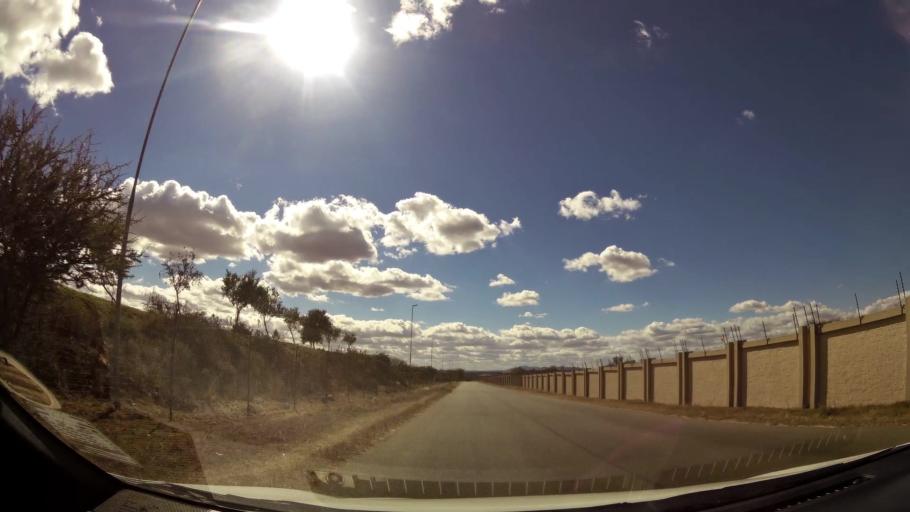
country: ZA
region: Limpopo
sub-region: Capricorn District Municipality
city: Polokwane
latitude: -23.8647
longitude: 29.5098
